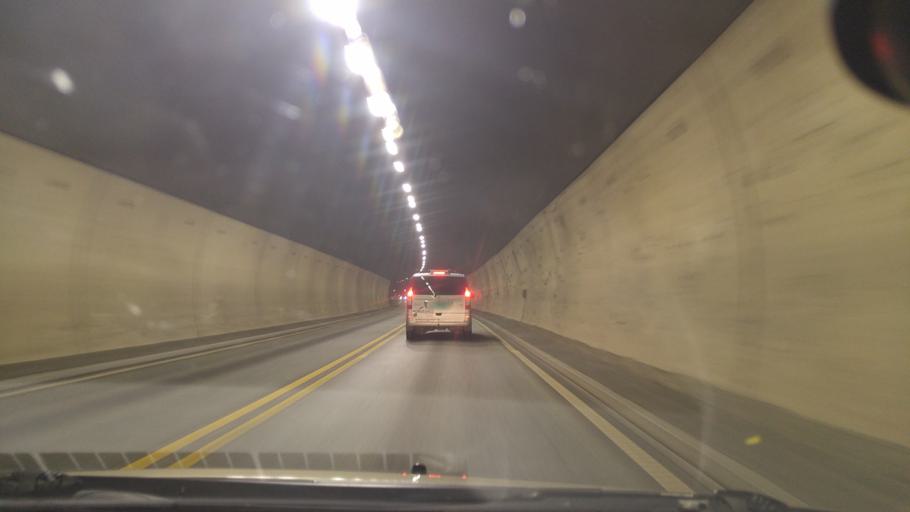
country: NO
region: Sor-Trondelag
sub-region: Malvik
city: Hommelvik
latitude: 63.4103
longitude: 10.7747
